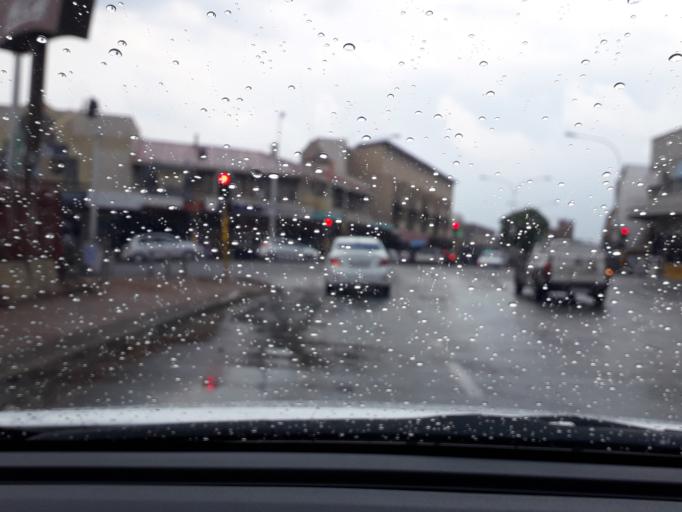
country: ZA
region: Gauteng
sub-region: City of Johannesburg Metropolitan Municipality
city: Johannesburg
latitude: -26.2427
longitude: 28.0529
